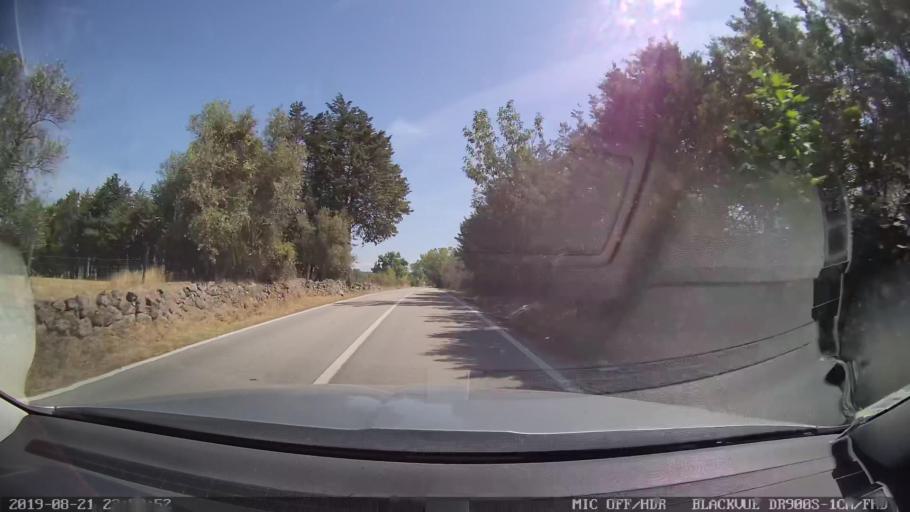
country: PT
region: Castelo Branco
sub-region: Idanha-A-Nova
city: Idanha-a-Nova
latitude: 39.8953
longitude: -7.2377
